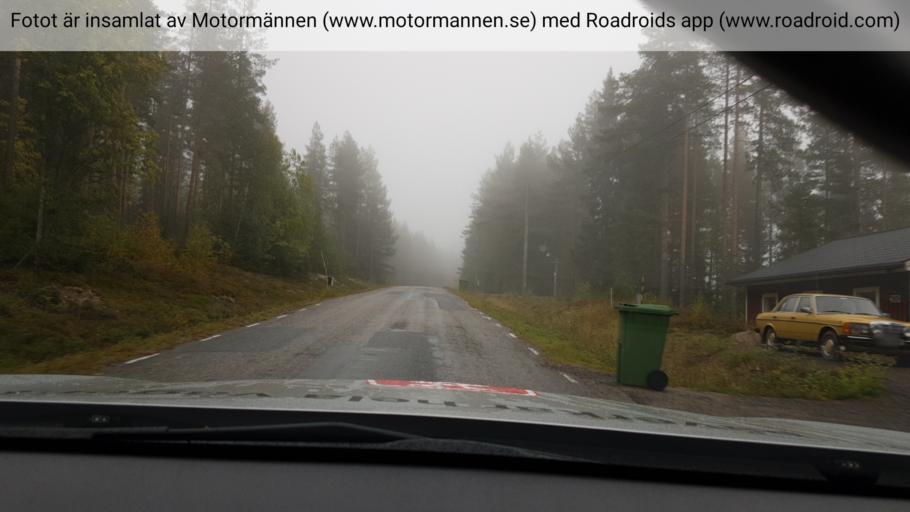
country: SE
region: Vaesterbotten
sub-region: Vannas Kommun
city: Vannasby
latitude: 64.0811
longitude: 20.0455
